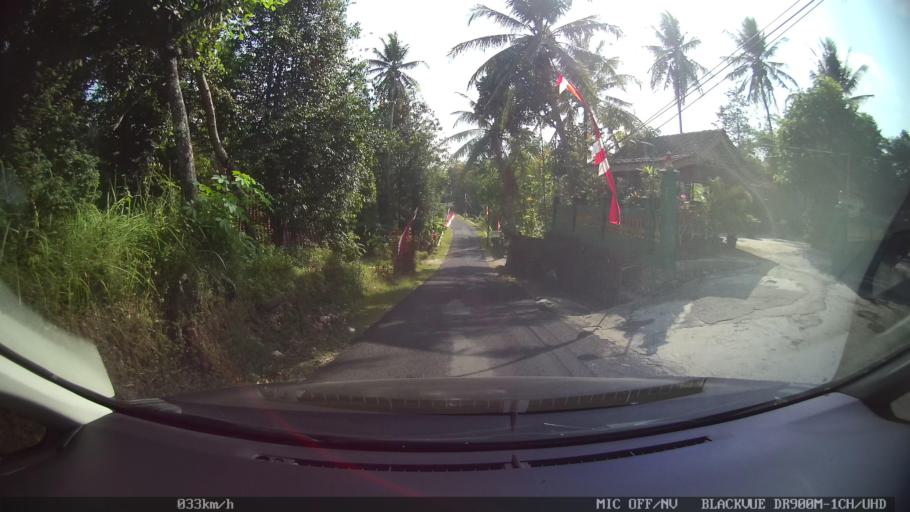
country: ID
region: Daerah Istimewa Yogyakarta
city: Kasihan
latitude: -7.8170
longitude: 110.2973
